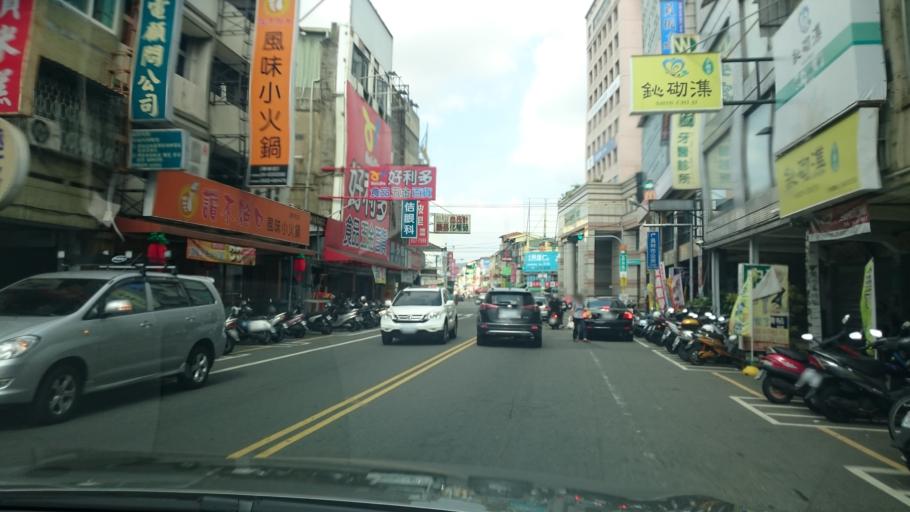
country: TW
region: Taiwan
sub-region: Nantou
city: Nantou
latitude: 23.9623
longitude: 120.5703
